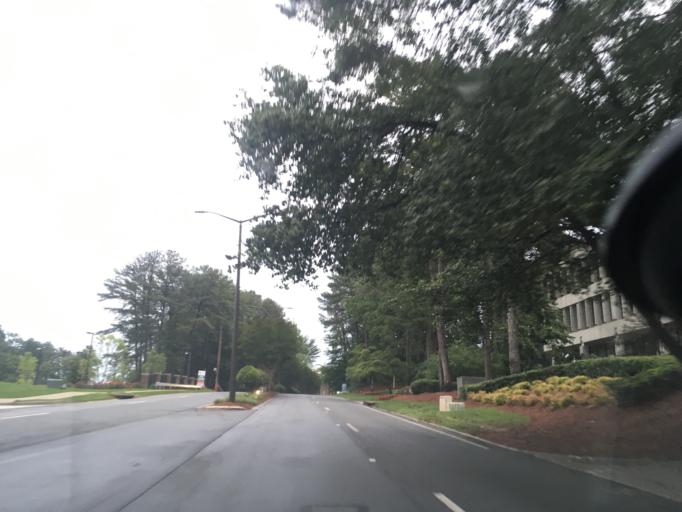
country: US
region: Georgia
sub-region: DeKalb County
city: North Druid Hills
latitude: 33.8295
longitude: -84.3373
